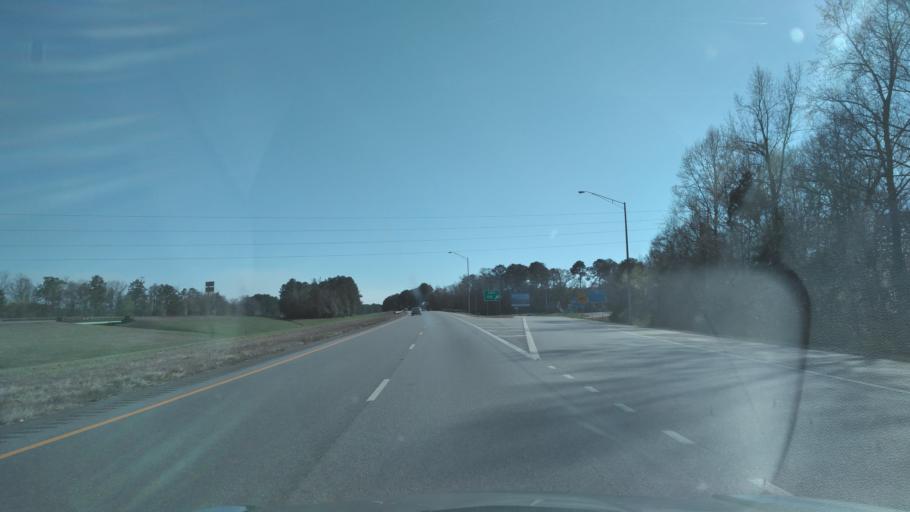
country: US
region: Alabama
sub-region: Butler County
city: Greenville
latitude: 31.8253
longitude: -86.6644
